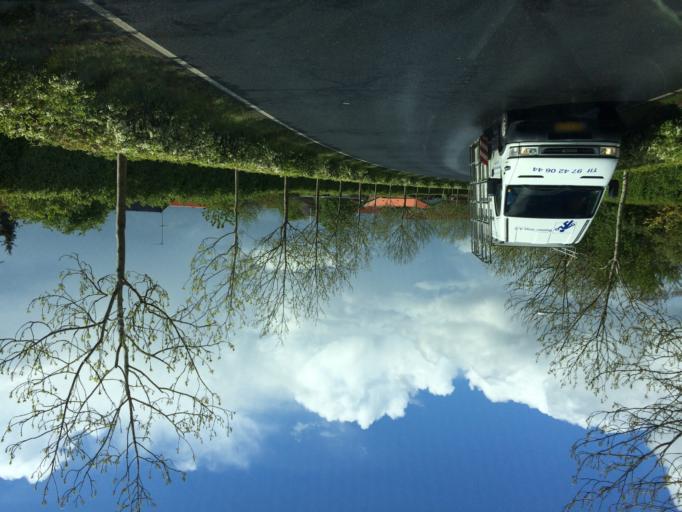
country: DK
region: Central Jutland
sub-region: Holstebro Kommune
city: Holstebro
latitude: 56.3512
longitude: 8.6049
